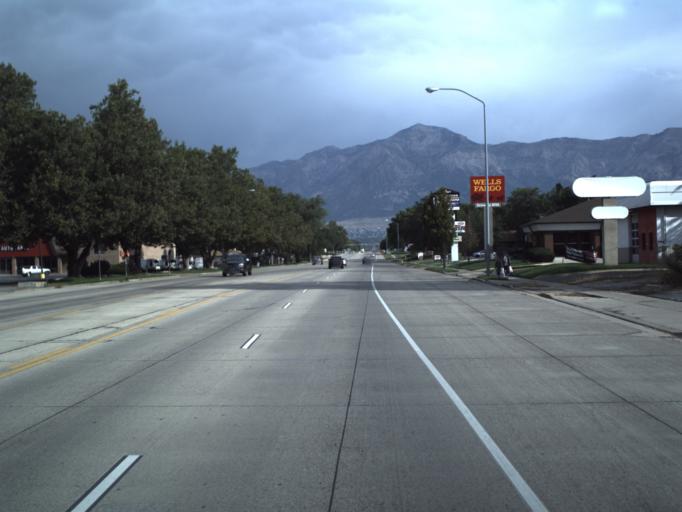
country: US
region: Utah
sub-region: Weber County
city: Harrisville
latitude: 41.2602
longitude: -111.9695
